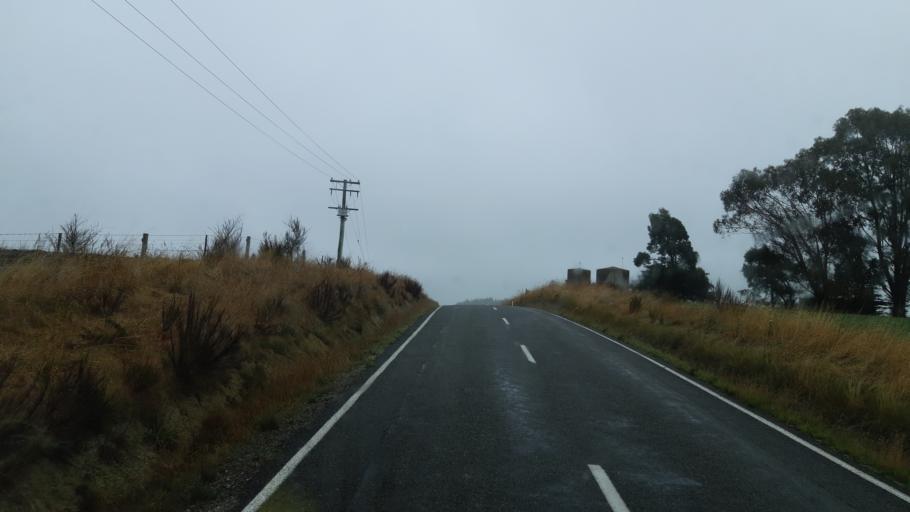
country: NZ
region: Otago
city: Oamaru
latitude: -44.9378
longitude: 170.7641
